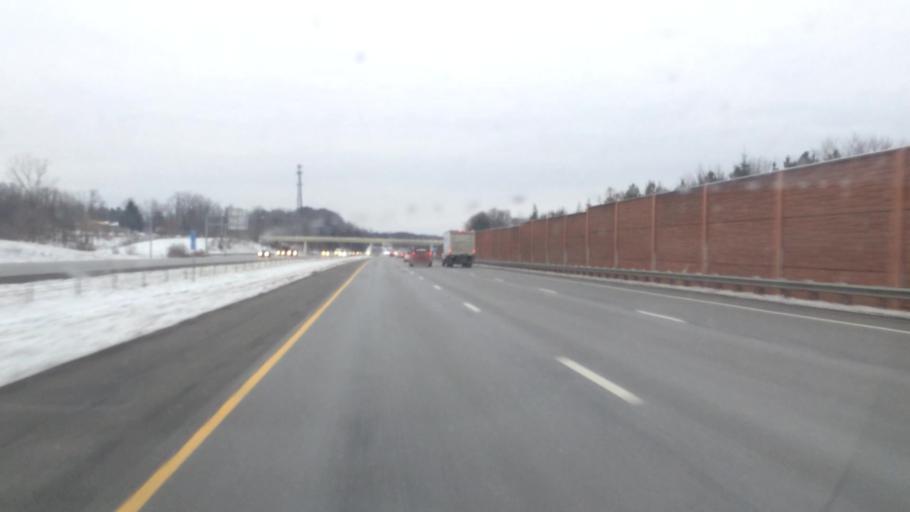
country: US
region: Ohio
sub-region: Medina County
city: Brunswick
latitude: 41.2299
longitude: -81.7955
